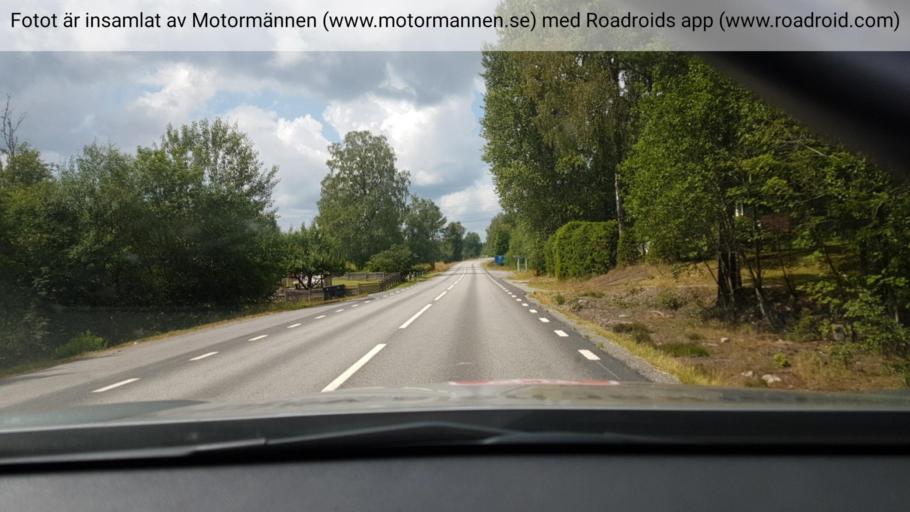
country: SE
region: Vaestra Goetaland
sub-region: Svenljunga Kommun
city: Svenljunga
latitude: 57.4849
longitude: 13.1398
